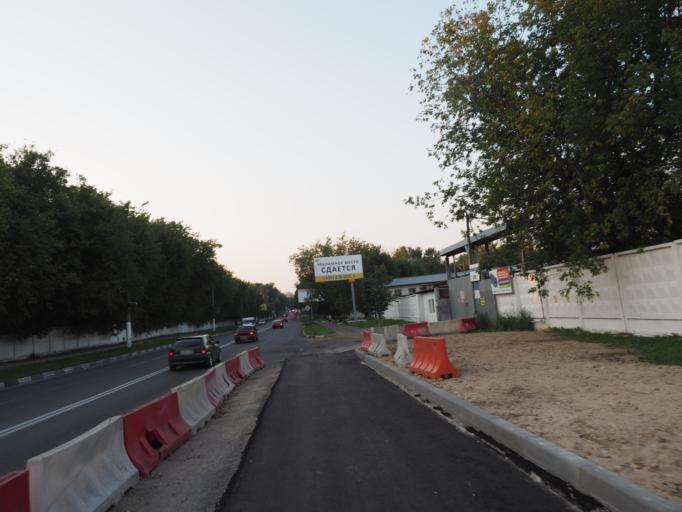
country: RU
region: Moskovskaya
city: Lyubertsy
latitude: 55.6703
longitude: 37.8892
